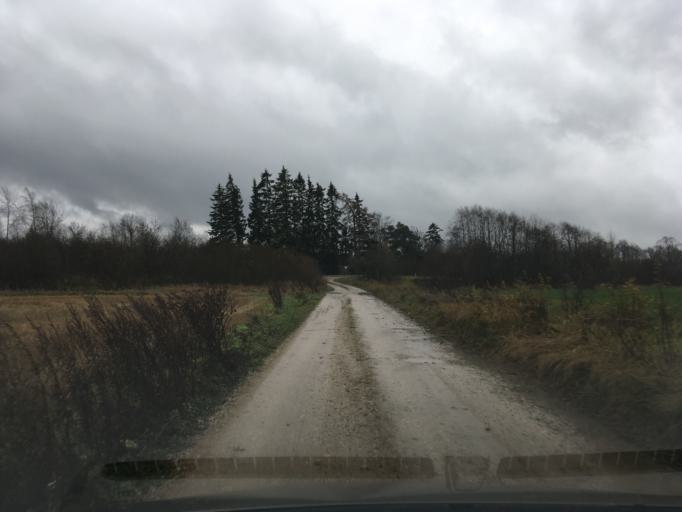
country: EE
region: Laeaene
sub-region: Lihula vald
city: Lihula
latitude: 58.7012
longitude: 23.8562
